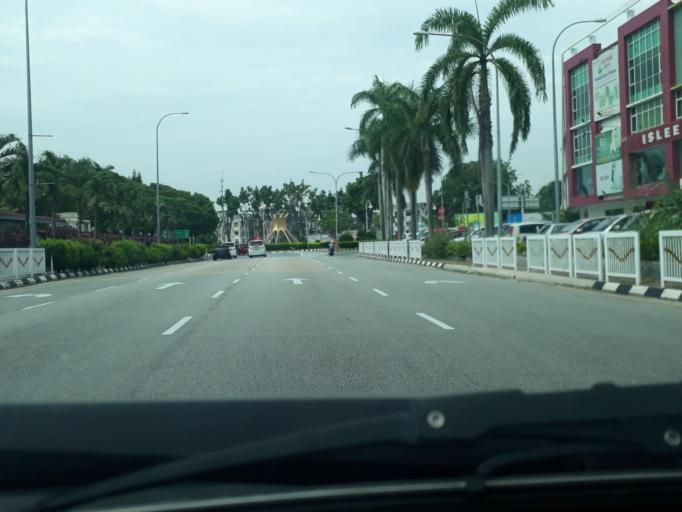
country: MY
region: Perak
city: Ipoh
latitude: 4.5933
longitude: 101.0901
